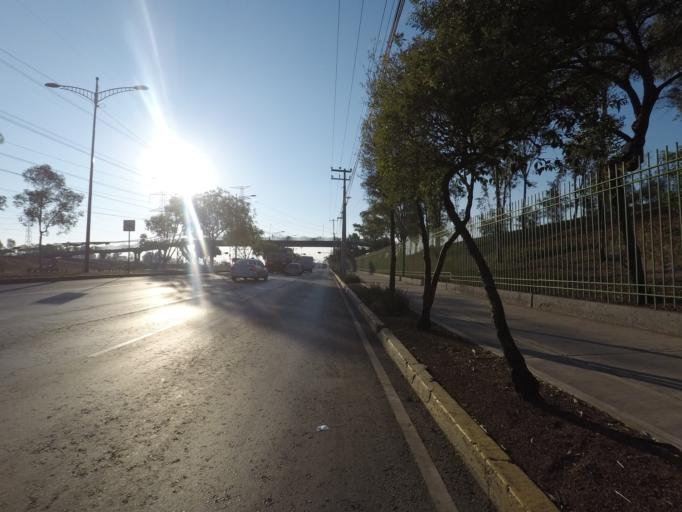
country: MX
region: Mexico City
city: Iztapalapa
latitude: 19.3617
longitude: -99.0465
